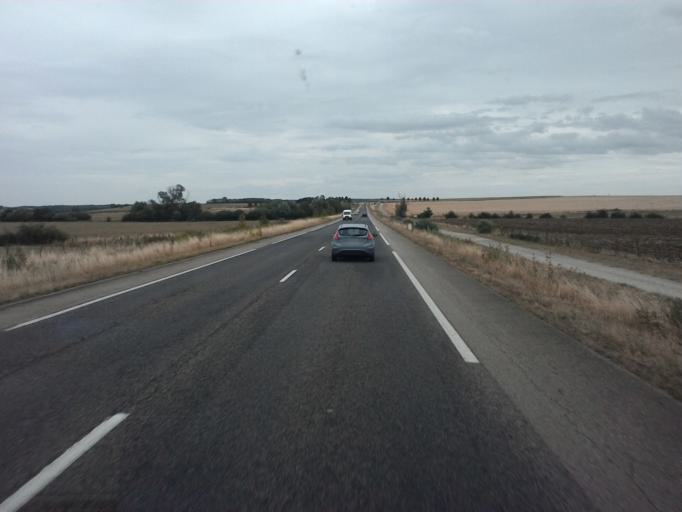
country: FR
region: Lorraine
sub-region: Departement de Meurthe-et-Moselle
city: Bainville-sur-Madon
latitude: 48.5776
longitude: 6.0640
